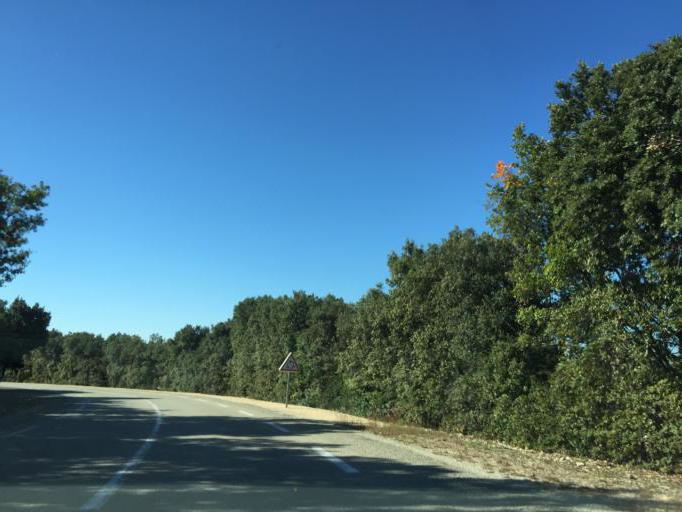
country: FR
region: Rhone-Alpes
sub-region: Departement de l'Ardeche
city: Ruoms
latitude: 44.4069
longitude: 4.4337
